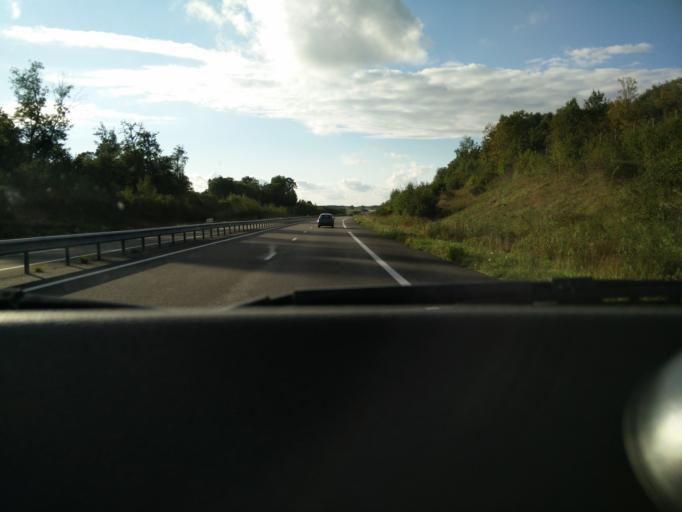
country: FR
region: Lorraine
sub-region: Departement de Meurthe-et-Moselle
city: Baccarat
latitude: 48.5171
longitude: 6.6505
